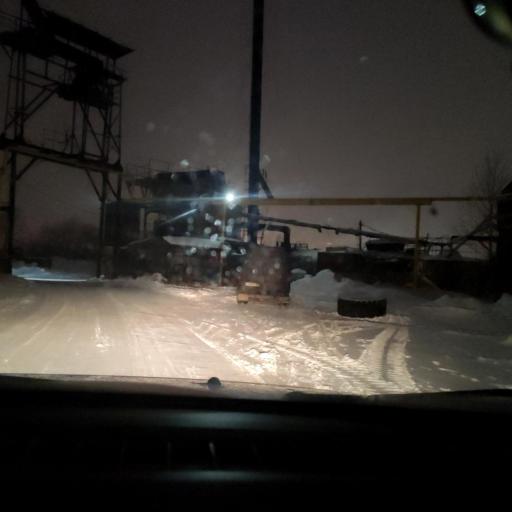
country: RU
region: Bashkortostan
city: Ufa
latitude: 54.8581
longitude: 56.0925
